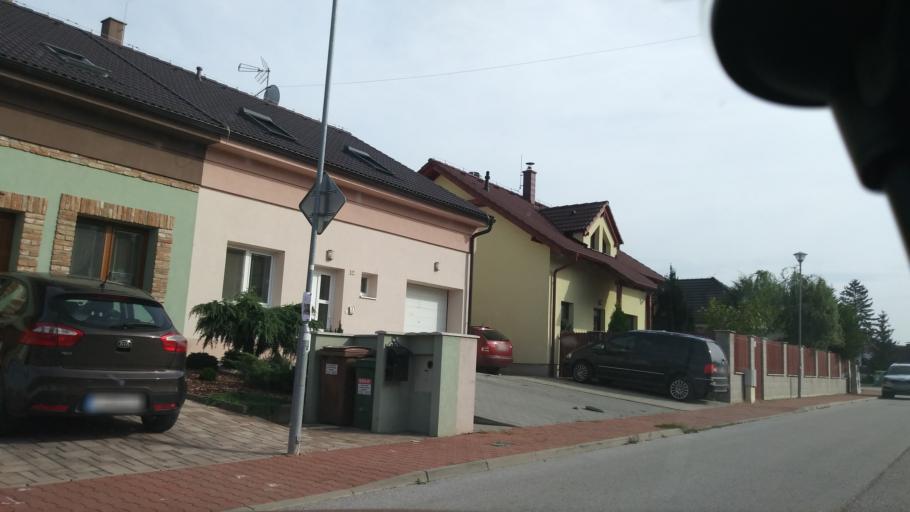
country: SK
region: Trnavsky
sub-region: Okres Skalica
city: Skalica
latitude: 48.8547
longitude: 17.2302
